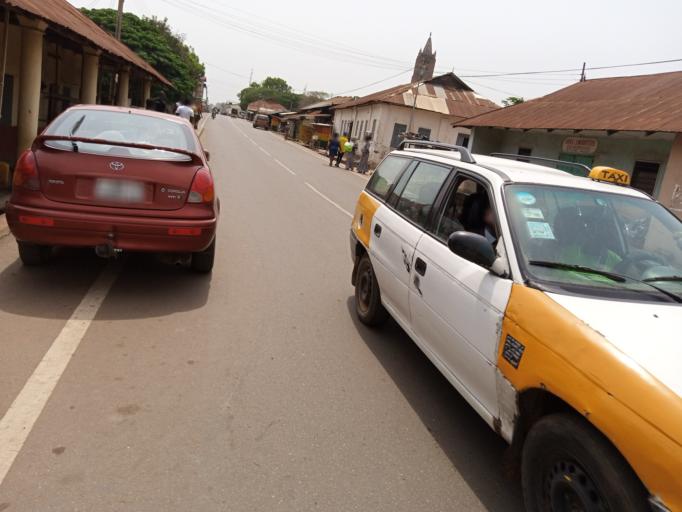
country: GH
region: Volta
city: Kpandu
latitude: 6.9992
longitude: 0.2943
